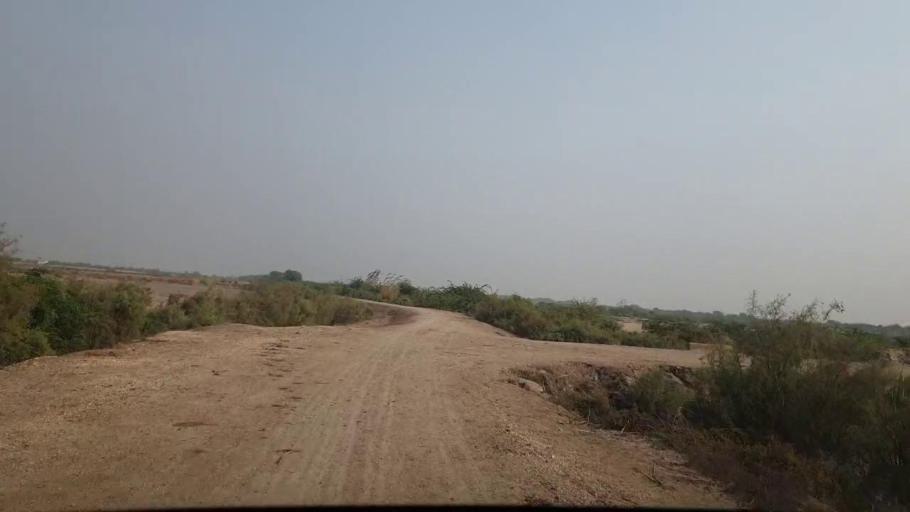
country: PK
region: Sindh
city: Jati
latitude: 24.2794
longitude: 68.4227
